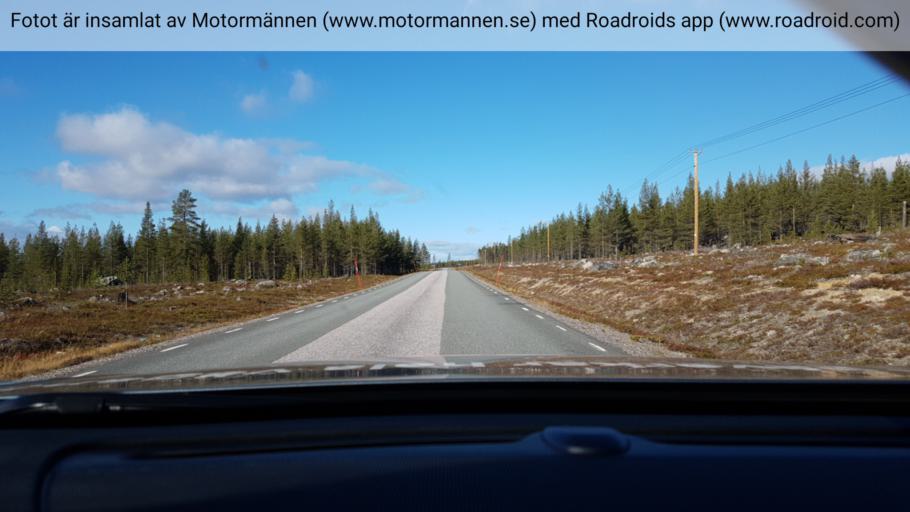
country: SE
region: Vaesterbotten
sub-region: Mala Kommun
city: Mala
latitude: 65.7734
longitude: 18.5258
